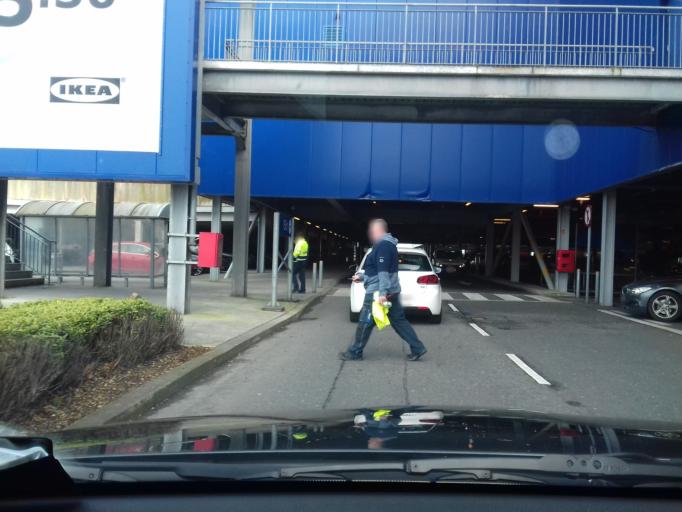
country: IE
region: Leinster
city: Ballymun
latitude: 53.4075
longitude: -6.2772
